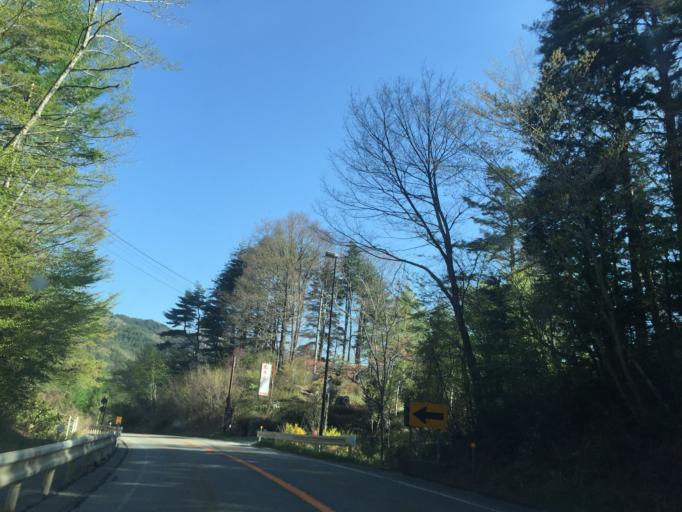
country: JP
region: Nagano
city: Iida
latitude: 35.3823
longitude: 137.6841
